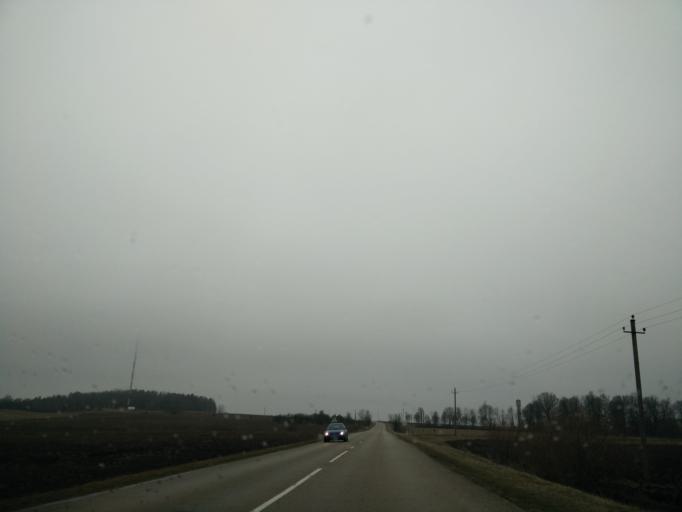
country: LT
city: Ariogala
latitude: 55.3436
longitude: 23.3936
